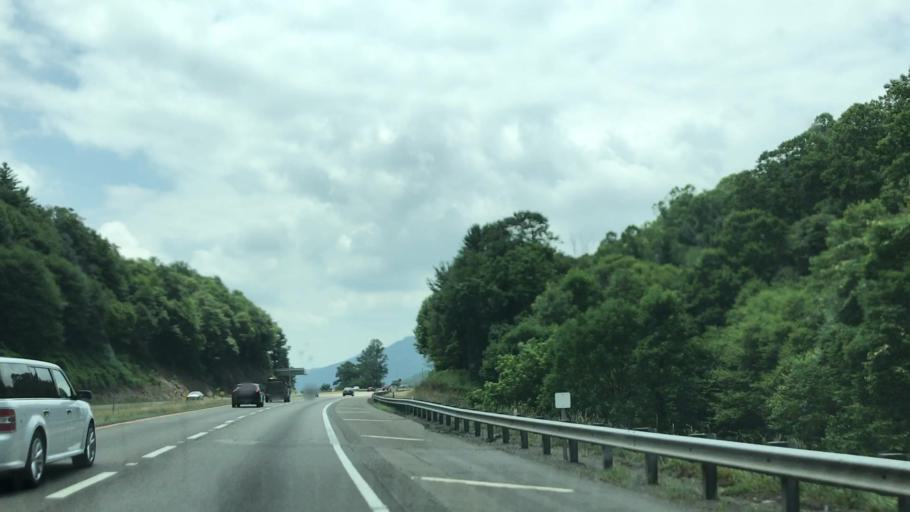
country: US
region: Virginia
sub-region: Carroll County
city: Cana
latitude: 36.6481
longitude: -80.7070
